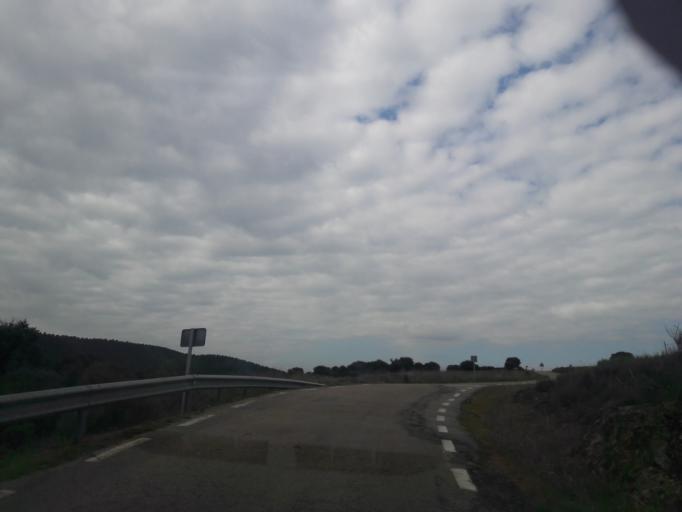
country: ES
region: Castille and Leon
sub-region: Provincia de Salamanca
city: Serradilla del Arroyo
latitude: 40.5226
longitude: -6.3736
